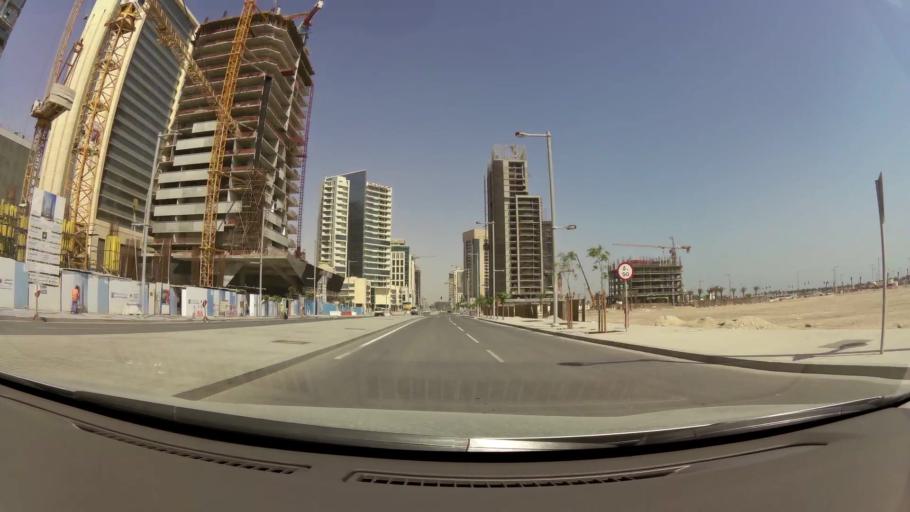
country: QA
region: Baladiyat ad Dawhah
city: Doha
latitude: 25.3888
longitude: 51.5241
